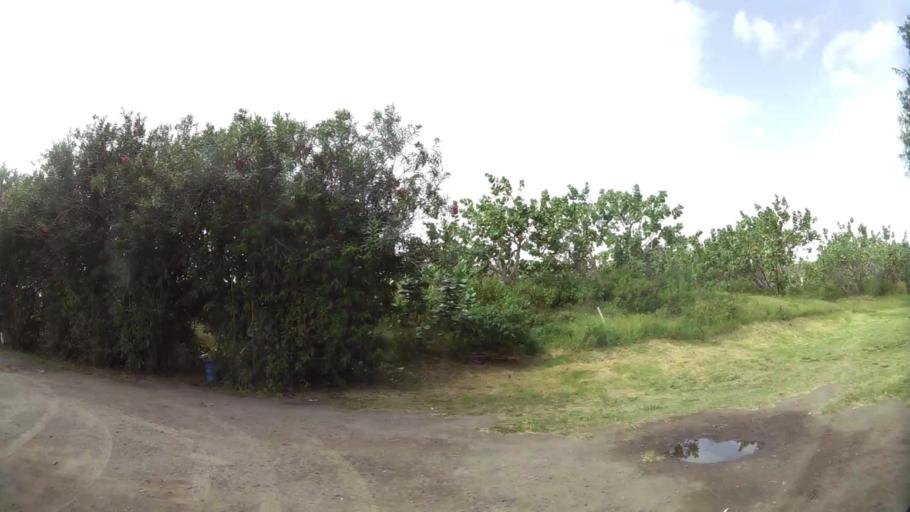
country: KN
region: Saint George Basseterre
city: Basseterre
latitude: 17.2880
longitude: -62.6860
